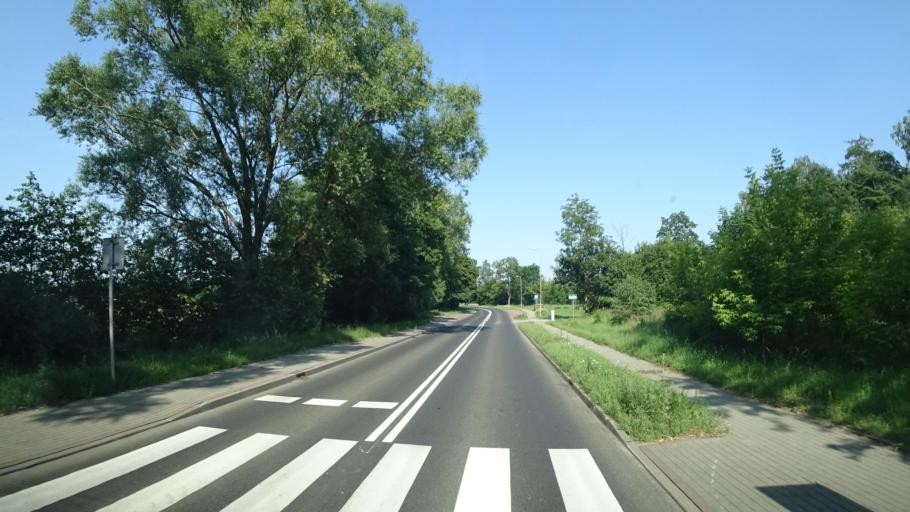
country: PL
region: West Pomeranian Voivodeship
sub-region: Powiat szczecinecki
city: Borne Sulinowo
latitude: 53.6284
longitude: 16.6049
